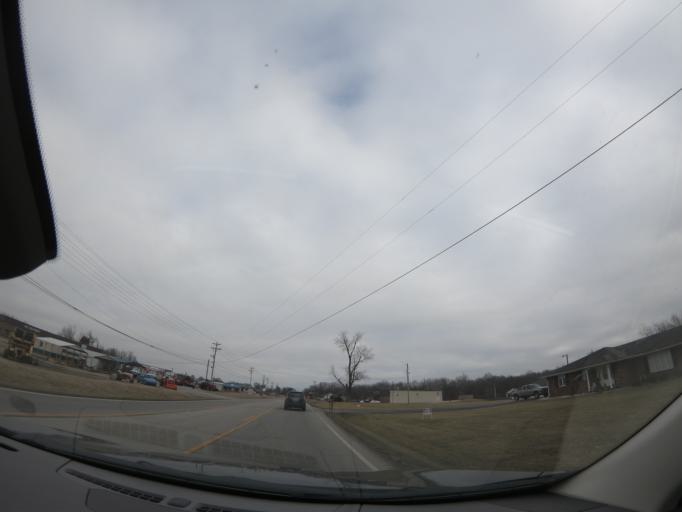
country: US
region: Kentucky
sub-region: Nelson County
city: Bardstown
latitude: 37.8247
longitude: -85.4397
